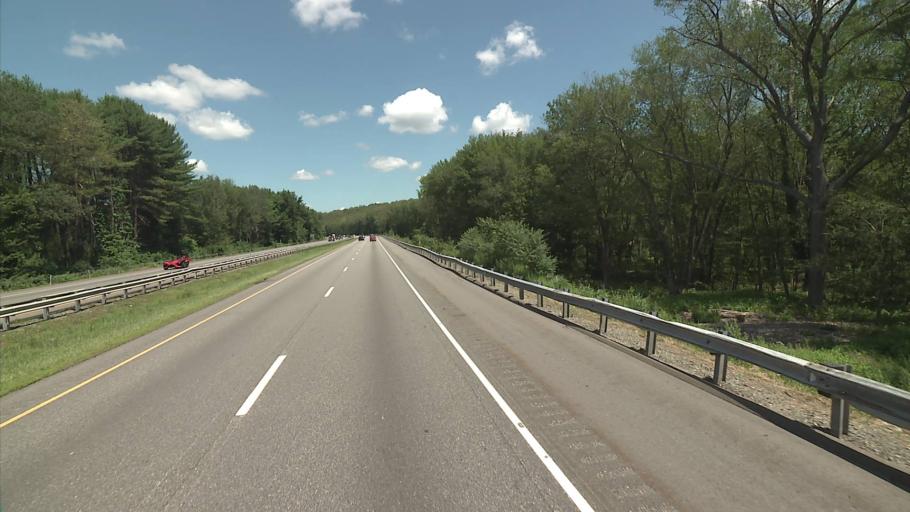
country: US
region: Connecticut
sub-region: New London County
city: Oxoboxo River
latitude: 41.4579
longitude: -72.1156
